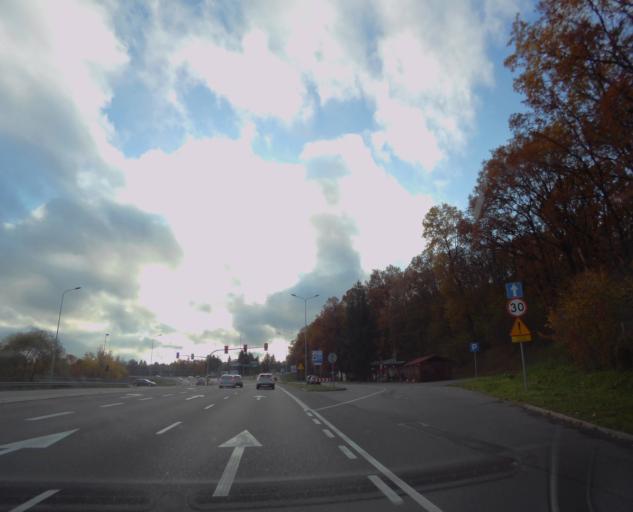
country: PL
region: Subcarpathian Voivodeship
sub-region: Powiat przemyski
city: Zurawica
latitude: 49.8105
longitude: 22.7786
